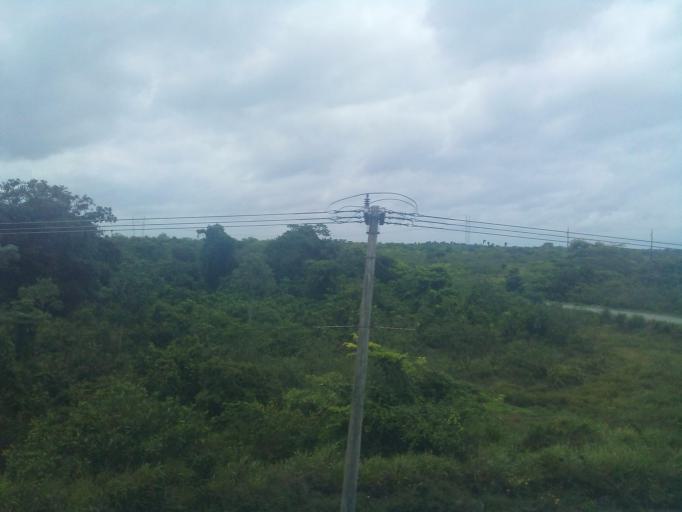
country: BR
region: Maranhao
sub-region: Arari
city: Arari
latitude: -3.5759
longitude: -44.7454
